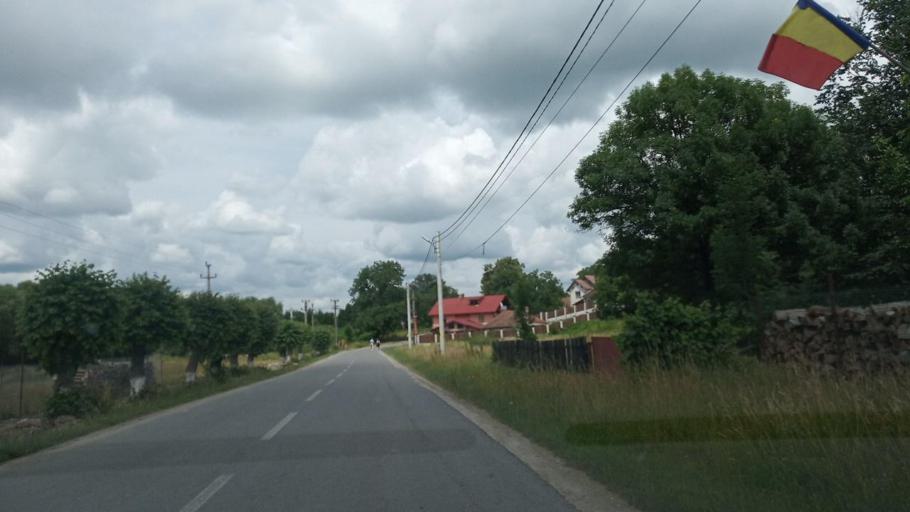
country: RO
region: Sibiu
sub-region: Comuna Cartisoara
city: Cartisoara
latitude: 45.7284
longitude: 24.5792
